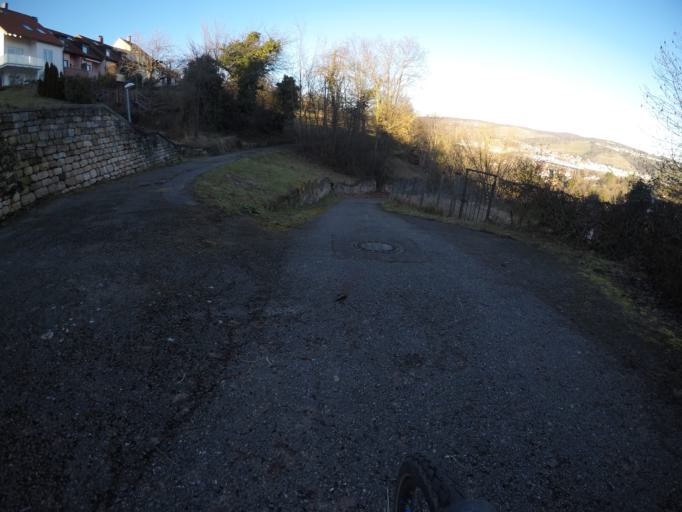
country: DE
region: Baden-Wuerttemberg
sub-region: Regierungsbezirk Stuttgart
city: Ostfildern
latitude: 48.7522
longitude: 9.2453
